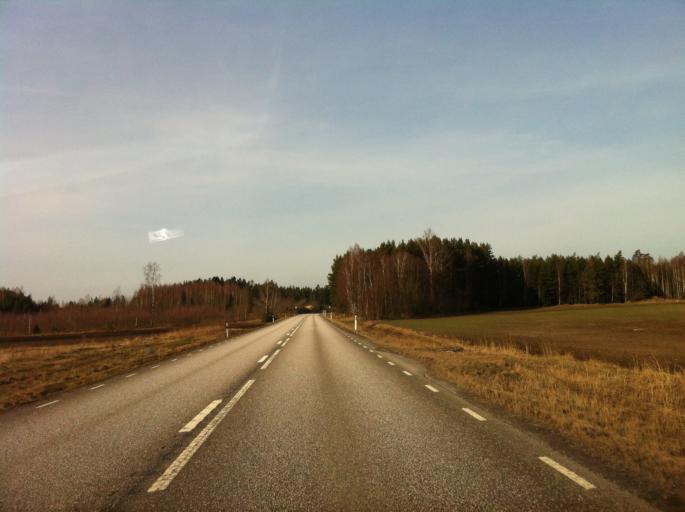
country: SE
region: Vaestra Goetaland
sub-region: Skovde Kommun
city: Skultorp
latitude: 58.2397
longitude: 13.8242
